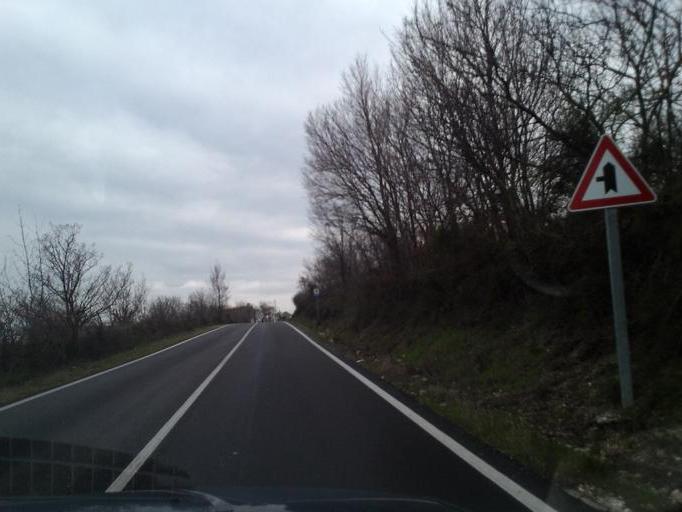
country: IT
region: Veneto
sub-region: Provincia di Verona
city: Montorio
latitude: 45.4983
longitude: 11.0761
